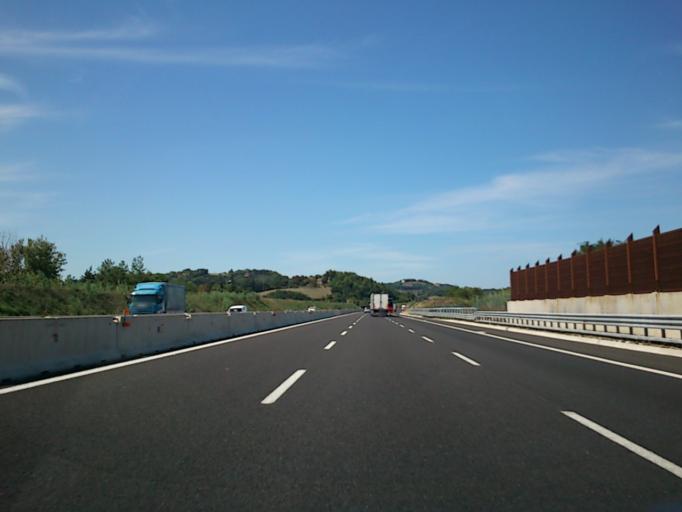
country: IT
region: The Marches
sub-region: Provincia di Pesaro e Urbino
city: Fenile
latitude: 43.8418
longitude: 12.9774
